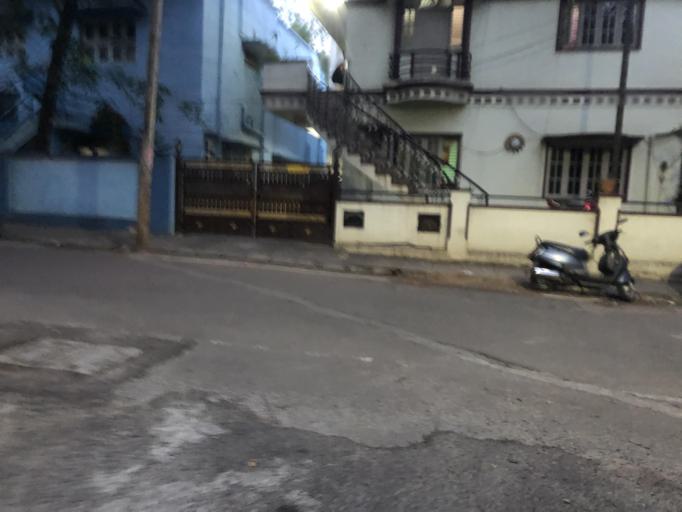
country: IN
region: Karnataka
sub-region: Bangalore Urban
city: Bangalore
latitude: 12.9392
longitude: 77.5425
